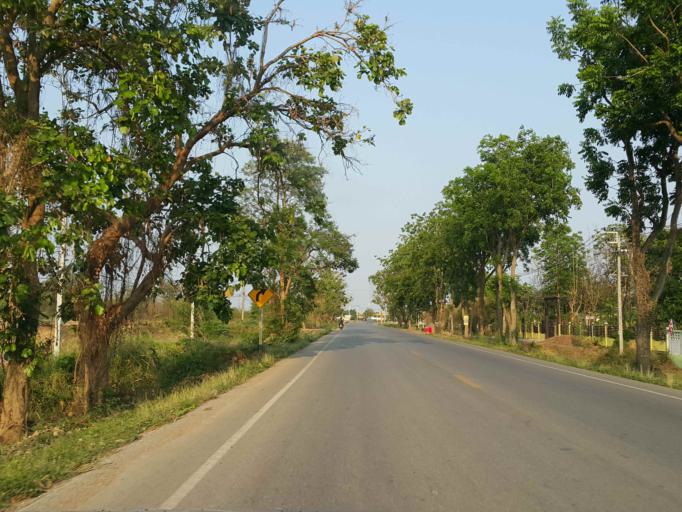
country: TH
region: Sukhothai
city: Sawankhalok
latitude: 17.3102
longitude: 99.7985
